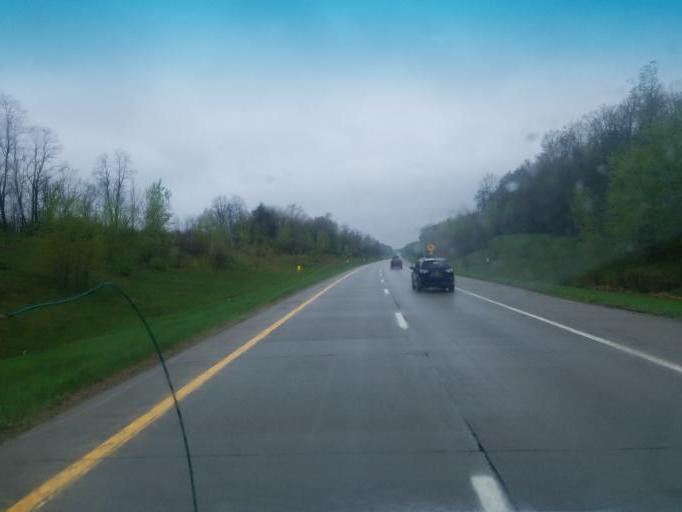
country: US
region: New York
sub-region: Chautauqua County
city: Mayville
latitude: 42.1534
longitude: -79.4418
